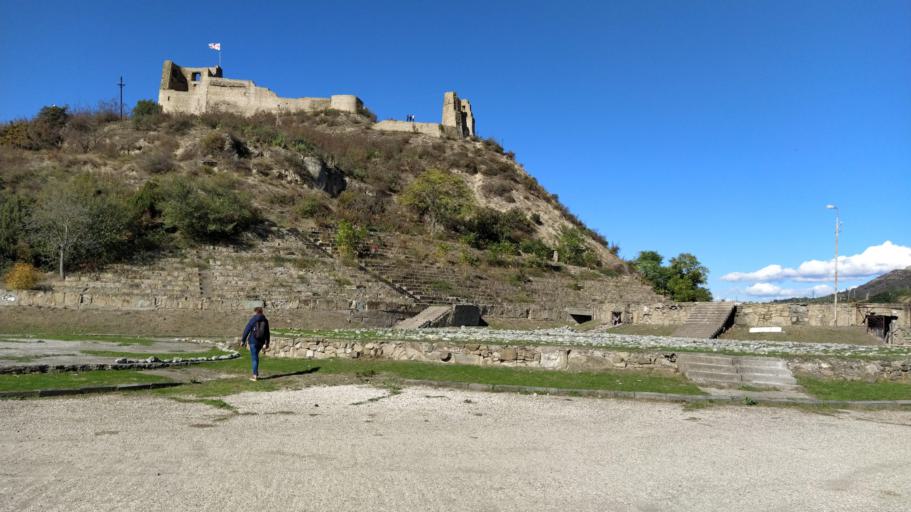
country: GE
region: Mtskheta-Mtianeti
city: Mtskheta
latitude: 41.8538
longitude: 44.7238
